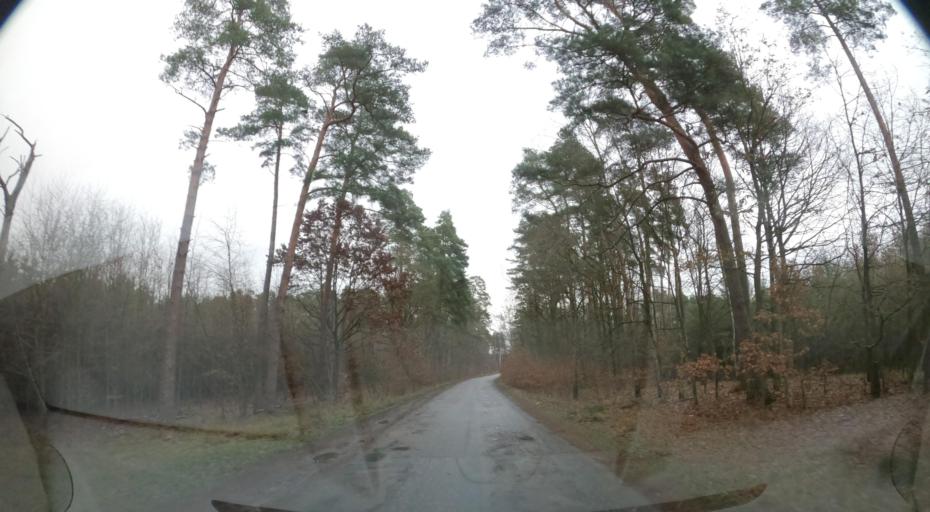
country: PL
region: Greater Poland Voivodeship
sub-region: Powiat zlotowski
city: Krajenka
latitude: 53.2872
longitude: 17.0381
